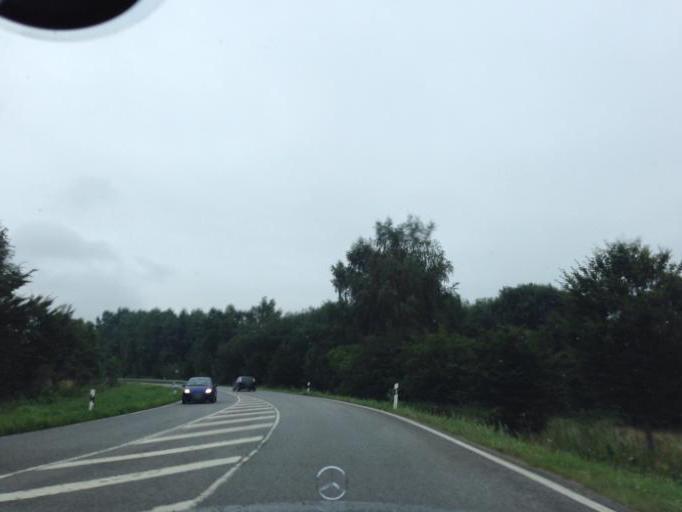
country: DE
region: Schleswig-Holstein
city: Barsbuettel
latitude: 53.5627
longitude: 10.1610
